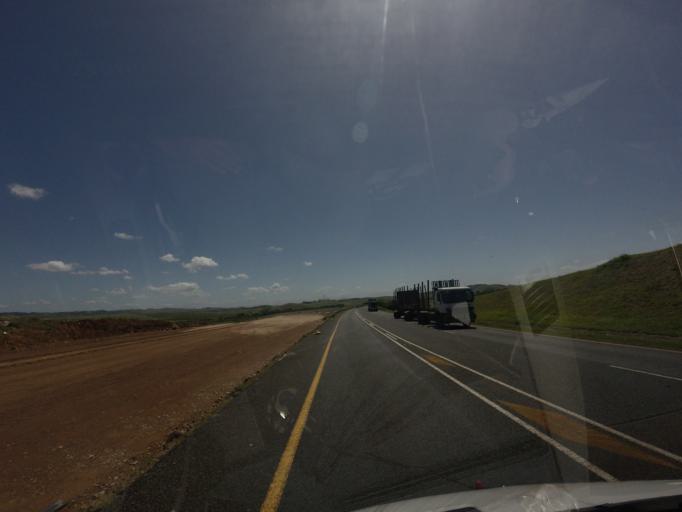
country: ZA
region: KwaZulu-Natal
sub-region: uThungulu District Municipality
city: eSikhawini
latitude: -28.9357
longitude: 31.7521
